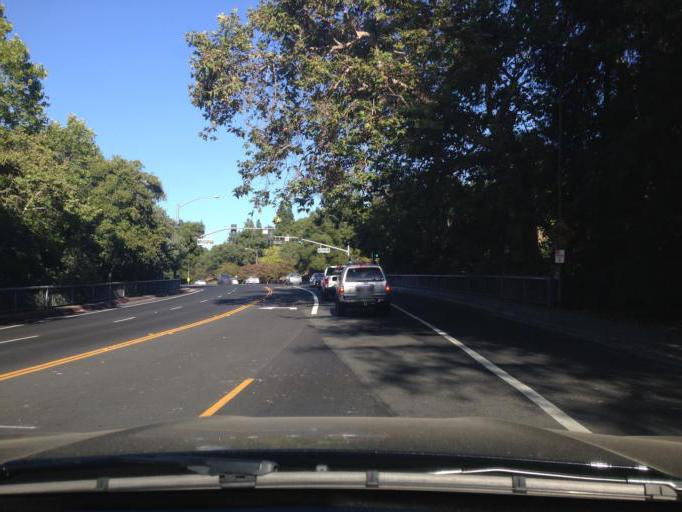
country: US
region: California
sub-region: Santa Clara County
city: Los Gatos
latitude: 37.2344
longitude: -121.9742
